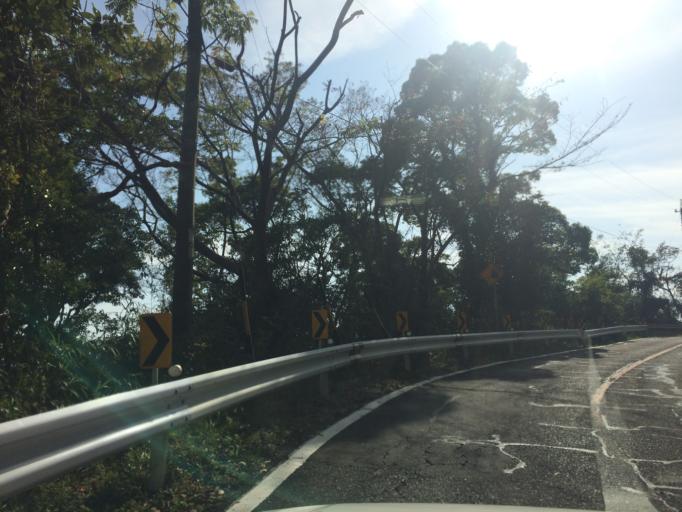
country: JP
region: Shizuoka
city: Yaizu
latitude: 34.9039
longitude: 138.3495
